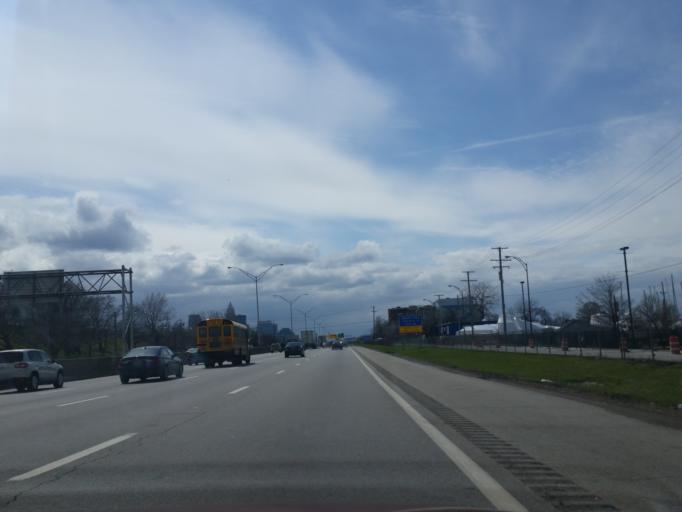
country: US
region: Ohio
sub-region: Cuyahoga County
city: Bratenahl
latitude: 41.5290
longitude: -81.6545
